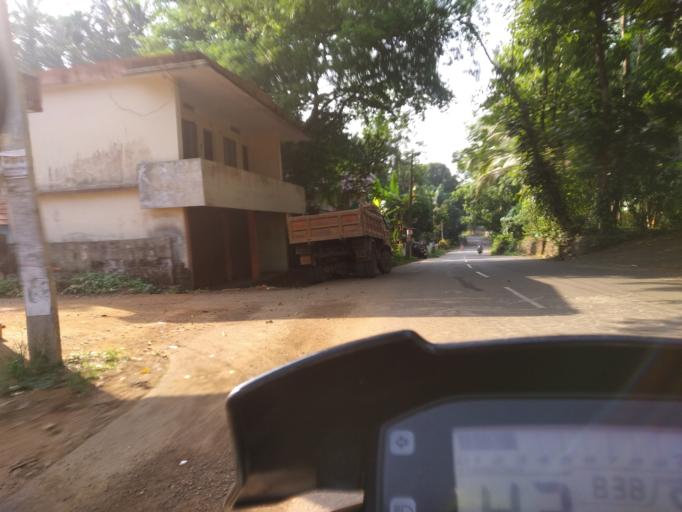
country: IN
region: Kerala
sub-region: Ernakulam
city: Ramamangalam
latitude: 9.9093
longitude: 76.4405
